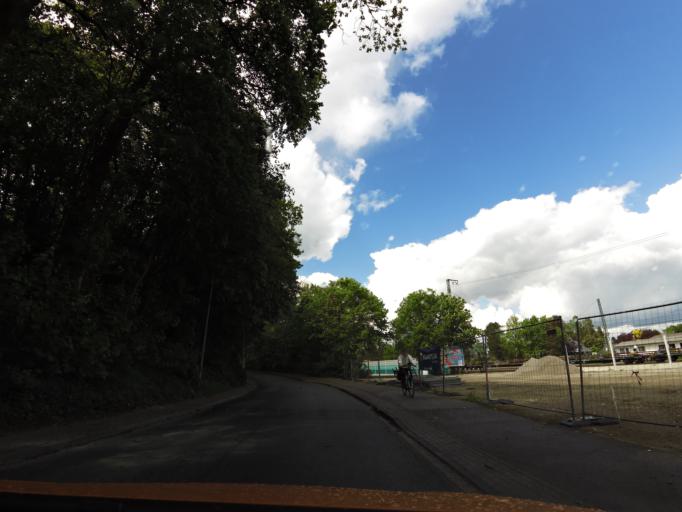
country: DE
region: Lower Saxony
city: Hude
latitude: 53.1062
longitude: 8.4672
